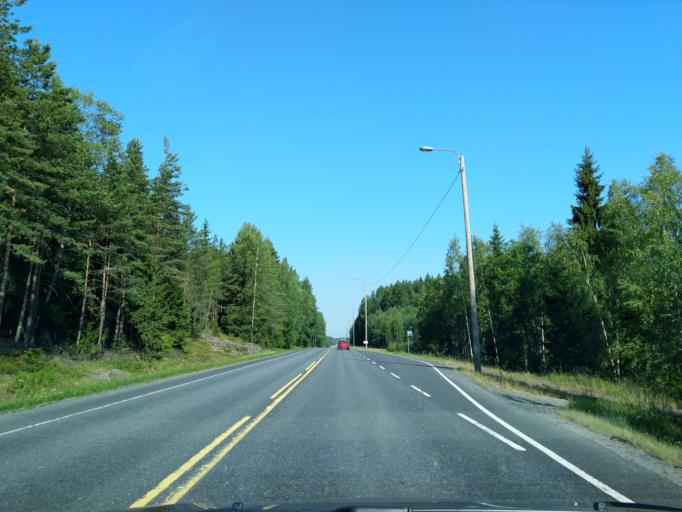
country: FI
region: Haeme
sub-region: Forssa
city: Forssa
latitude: 60.7936
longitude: 23.6385
